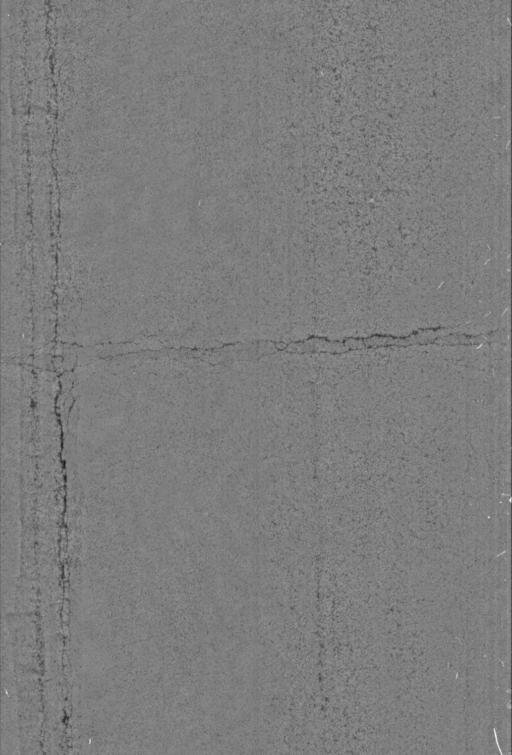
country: US
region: Washington, D.C.
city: Washington, D.C.
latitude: 38.8736
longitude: -77.0137
